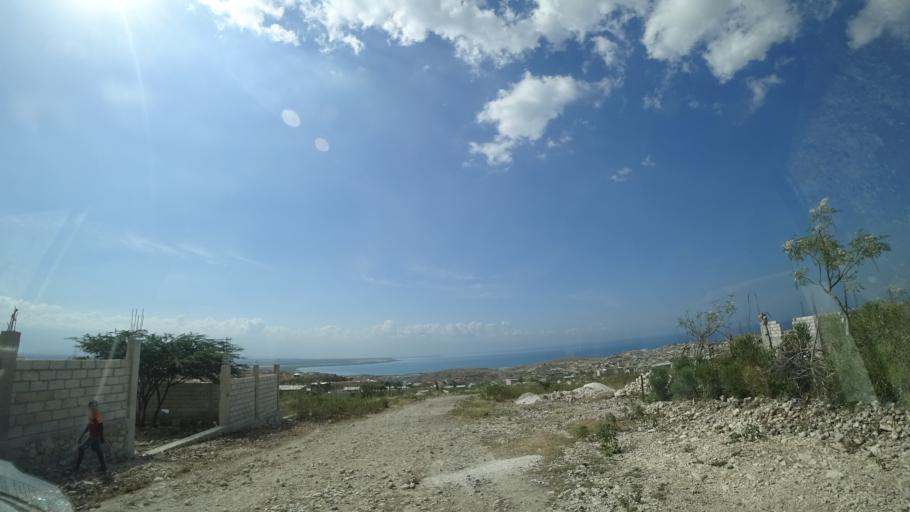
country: HT
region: Ouest
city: Cabaret
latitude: 18.6904
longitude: -72.3103
